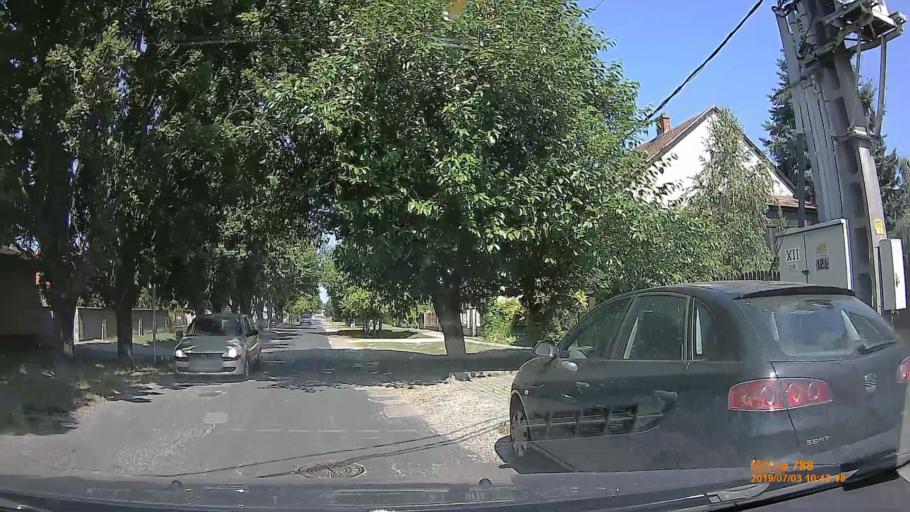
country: HU
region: Gyor-Moson-Sopron
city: Gyorujbarat
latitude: 47.6378
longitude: 17.6136
